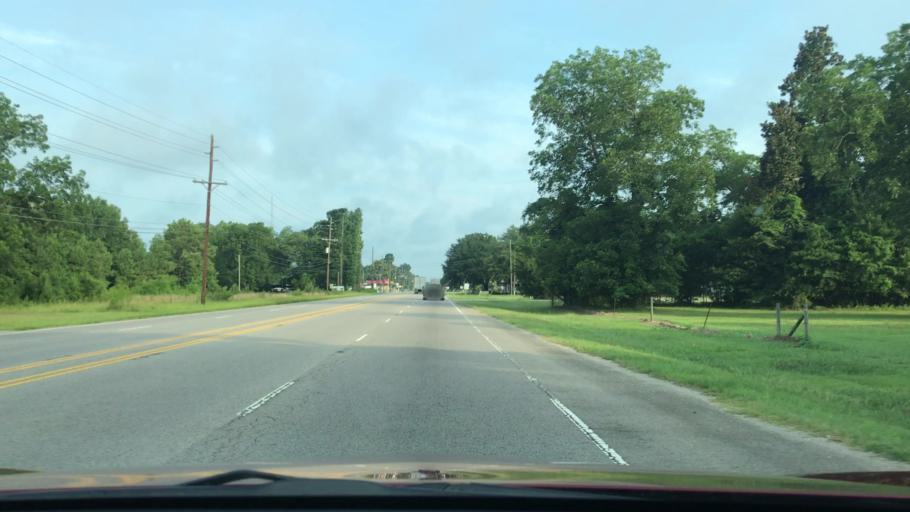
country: US
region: South Carolina
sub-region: Orangeburg County
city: Brookdale
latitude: 33.4751
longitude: -80.8125
